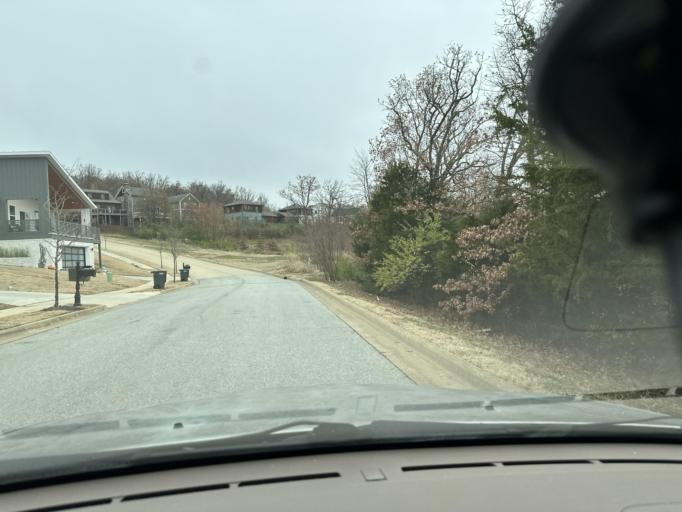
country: US
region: Arkansas
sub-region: Washington County
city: Fayetteville
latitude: 36.0948
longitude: -94.1511
